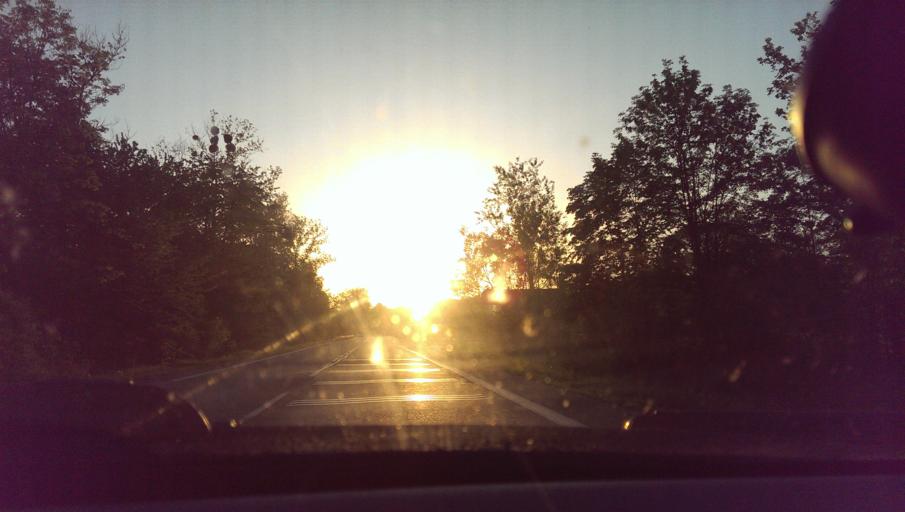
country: CZ
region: Zlin
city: Zasova
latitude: 49.4743
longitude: 18.0114
